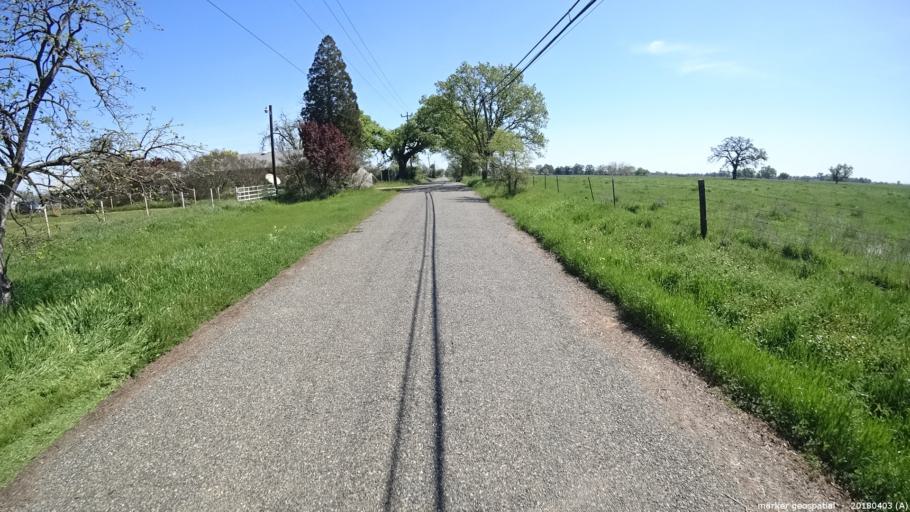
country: US
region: California
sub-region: Sacramento County
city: Wilton
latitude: 38.3952
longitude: -121.2898
